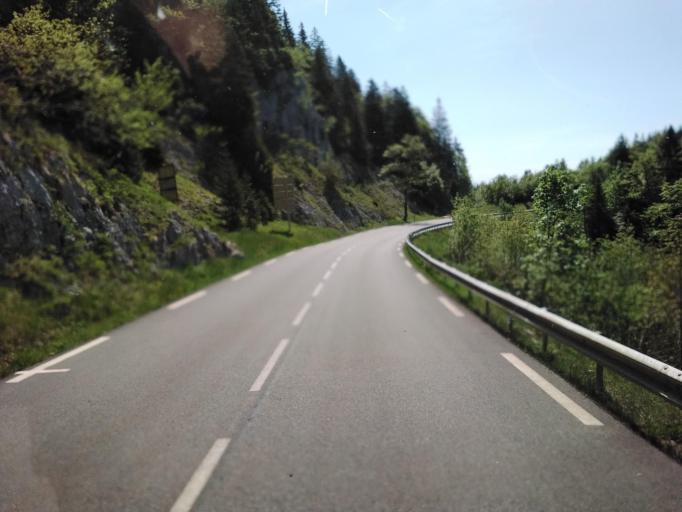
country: FR
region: Rhone-Alpes
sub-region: Departement de l'Ain
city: Gex
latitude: 46.3684
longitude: 6.0213
